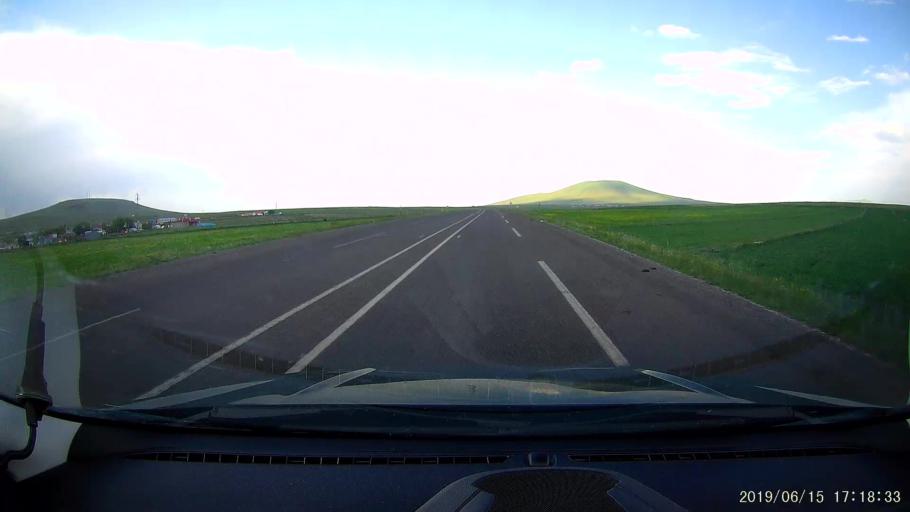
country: TR
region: Kars
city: Kars
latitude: 40.6130
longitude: 43.2603
